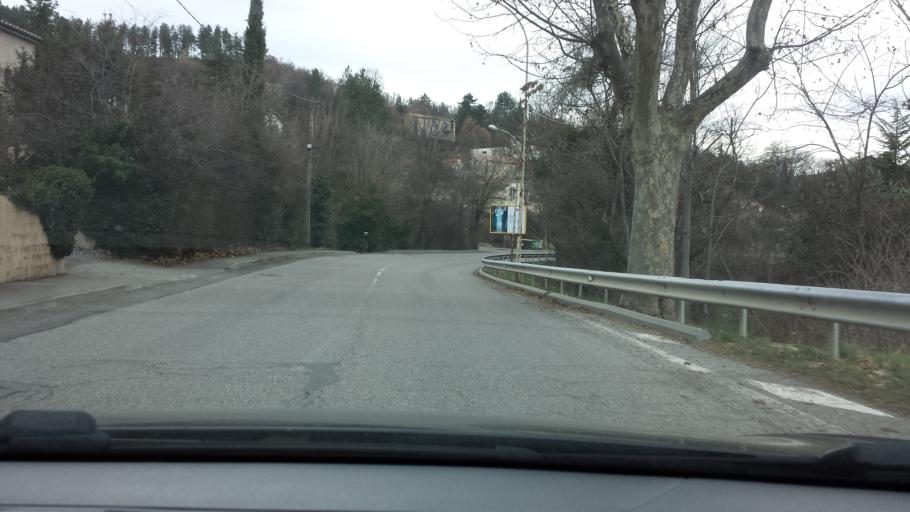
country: FR
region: Provence-Alpes-Cote d'Azur
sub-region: Departement des Alpes-de-Haute-Provence
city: Digne-les-Bains
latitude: 44.0816
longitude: 6.2235
